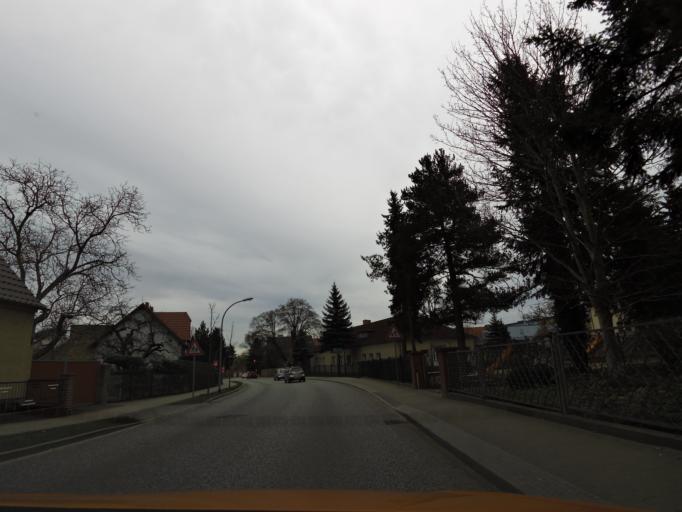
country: DE
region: Brandenburg
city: Belzig
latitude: 52.1439
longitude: 12.5874
